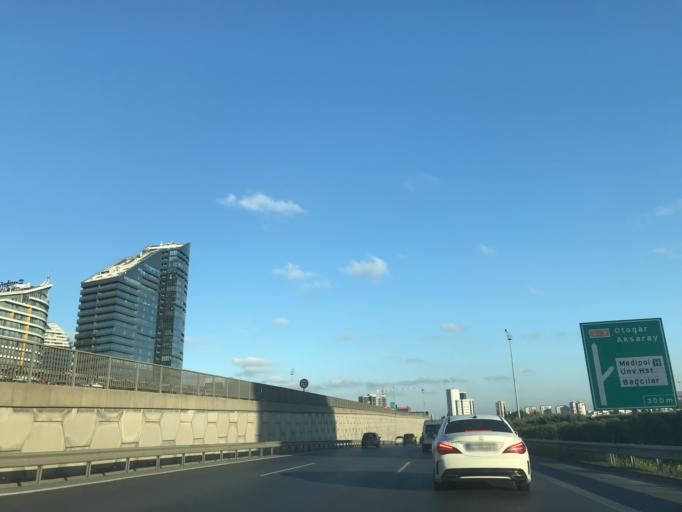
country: TR
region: Istanbul
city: Mahmutbey
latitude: 41.0627
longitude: 28.8389
